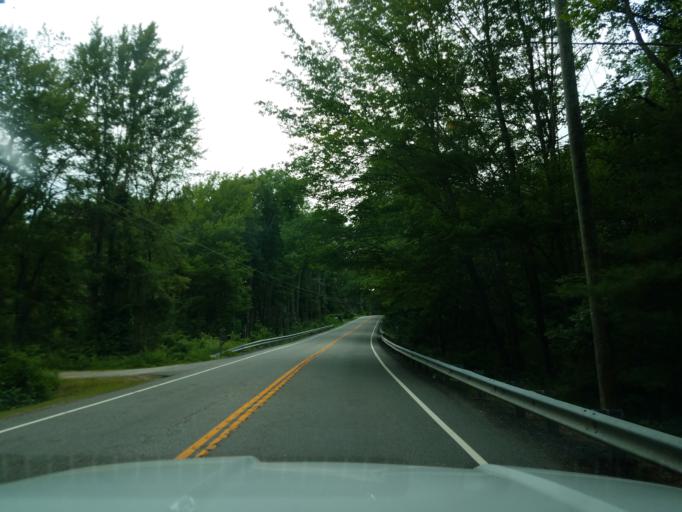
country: US
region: Massachusetts
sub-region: Worcester County
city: Southbridge
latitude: 42.0209
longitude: -72.0753
